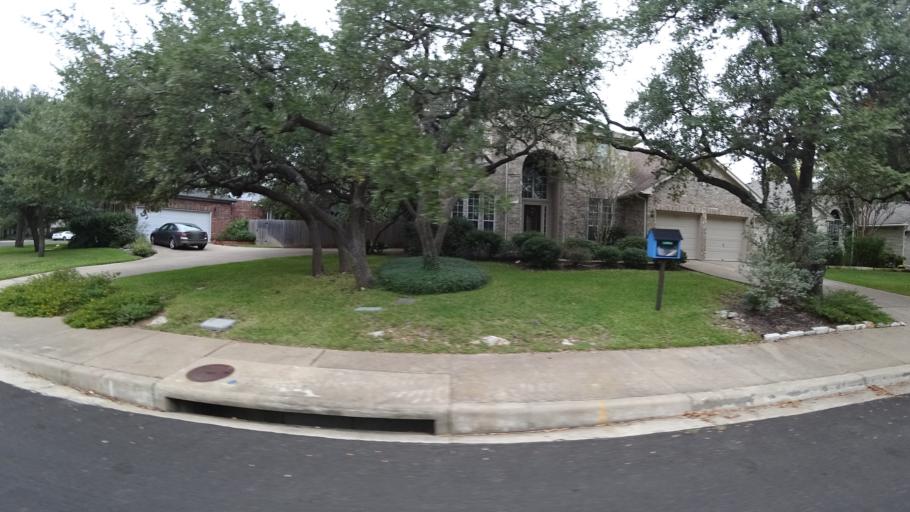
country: US
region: Texas
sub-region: Travis County
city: Shady Hollow
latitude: 30.1811
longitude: -97.8925
